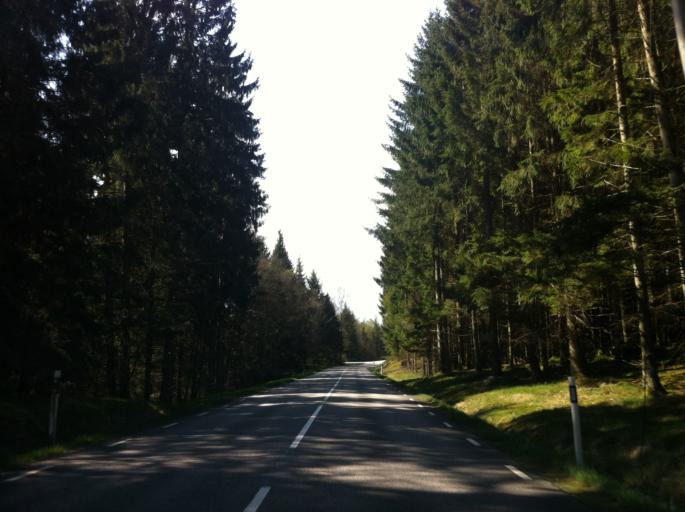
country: SE
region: Vaestra Goetaland
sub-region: Marks Kommun
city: Kinna
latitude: 57.1761
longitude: 12.7697
